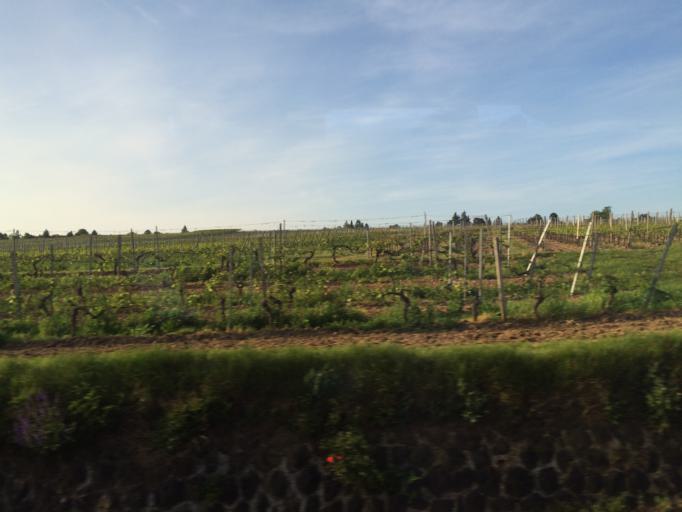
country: DE
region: Hesse
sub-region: Regierungsbezirk Darmstadt
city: Hochheim am Main
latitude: 50.0038
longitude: 8.3590
